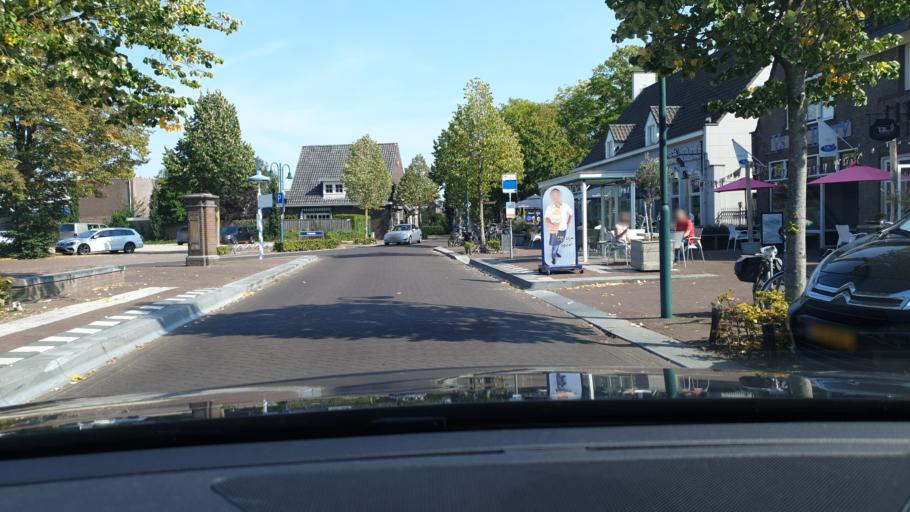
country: NL
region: North Brabant
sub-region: Gemeente Laarbeek
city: Aarle-Rixtel
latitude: 51.5178
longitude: 5.5951
